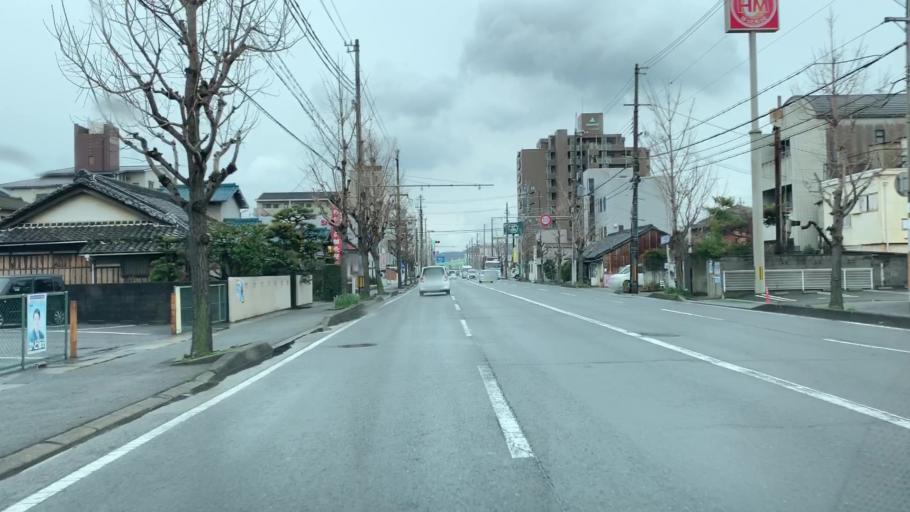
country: JP
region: Wakayama
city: Wakayama-shi
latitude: 34.2224
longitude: 135.1596
